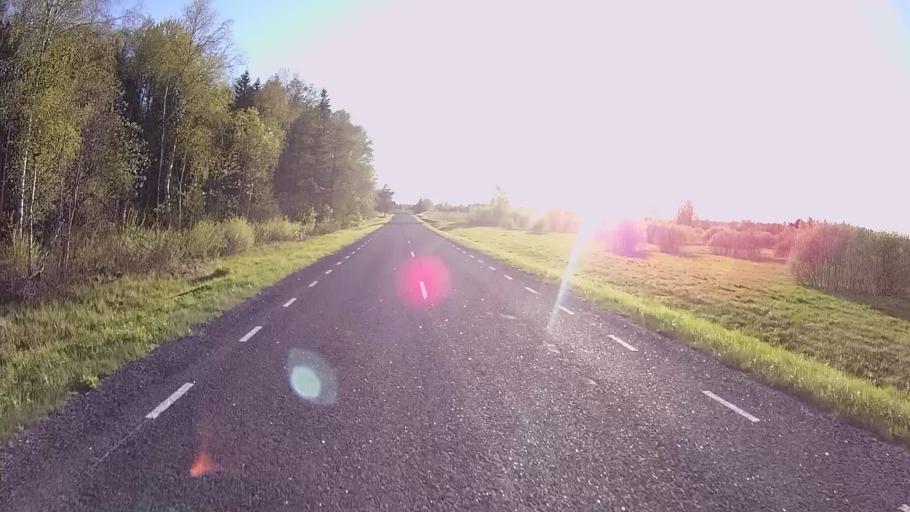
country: EE
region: Jogevamaa
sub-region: Poltsamaa linn
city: Poltsamaa
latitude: 58.5218
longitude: 25.9798
